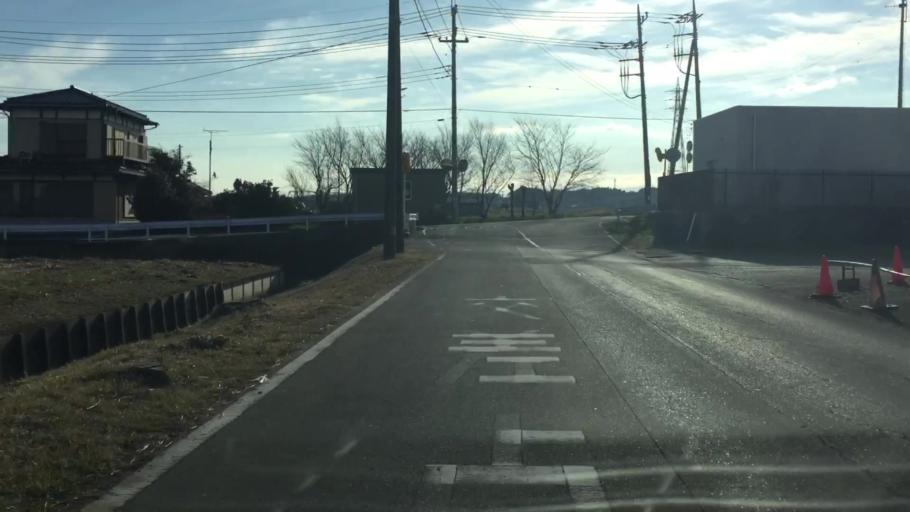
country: JP
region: Ibaraki
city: Toride
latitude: 35.8416
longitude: 140.1303
